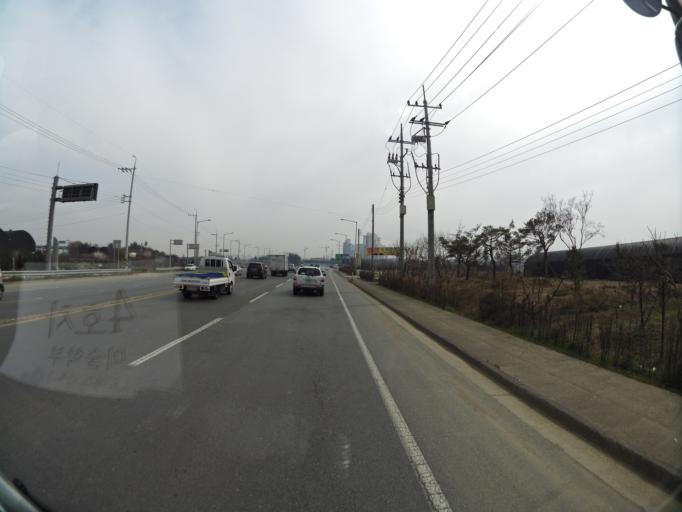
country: KR
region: Gyeongsangbuk-do
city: Hayang
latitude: 35.8736
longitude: 128.7912
